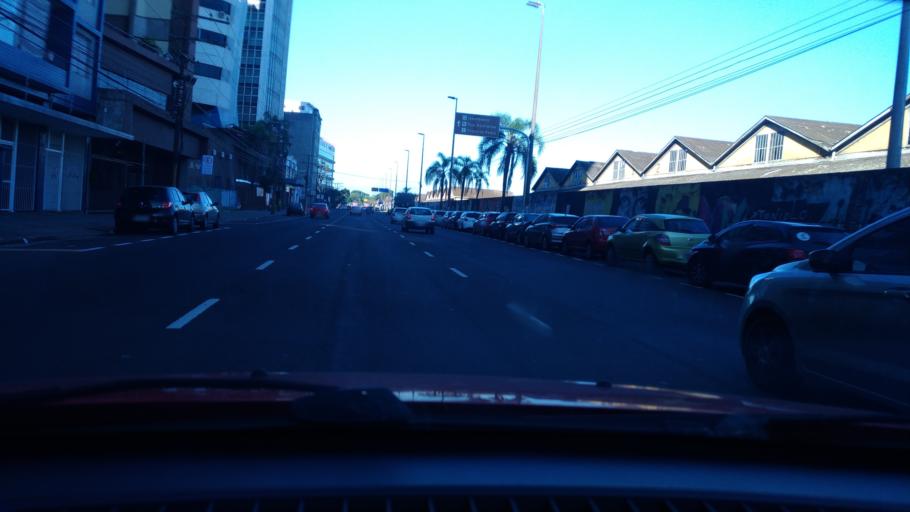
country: BR
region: Rio Grande do Sul
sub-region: Porto Alegre
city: Porto Alegre
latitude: -30.0286
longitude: -51.2334
